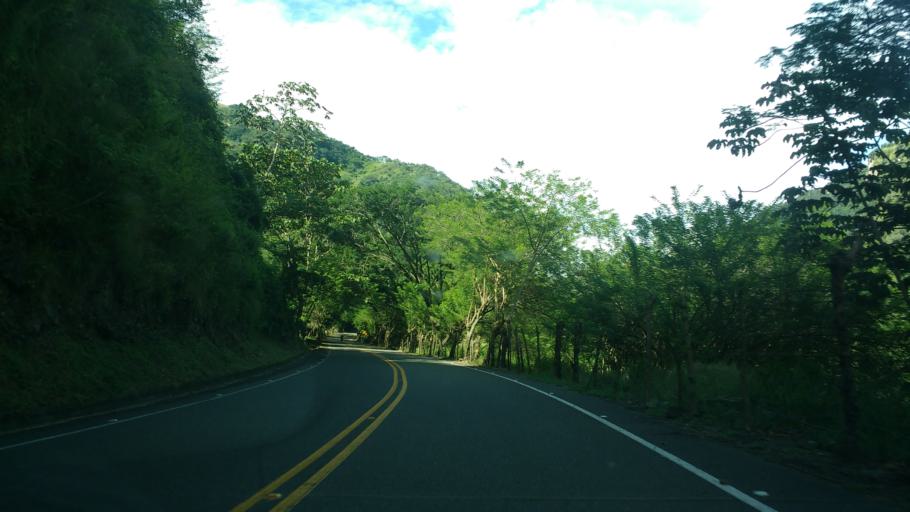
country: CO
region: Antioquia
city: Concordia
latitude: 6.0751
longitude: -75.8611
